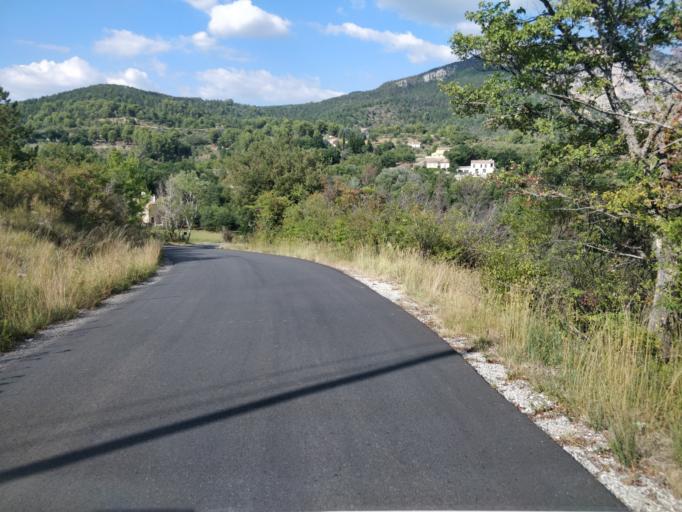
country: FR
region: Provence-Alpes-Cote d'Azur
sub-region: Departement des Alpes-de-Haute-Provence
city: Riez
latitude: 43.8408
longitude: 6.2078
